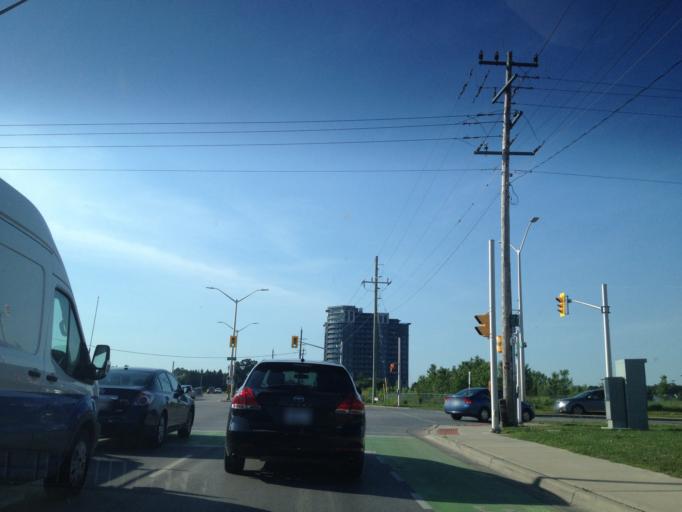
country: CA
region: Ontario
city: London
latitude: 43.0101
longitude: -81.3376
